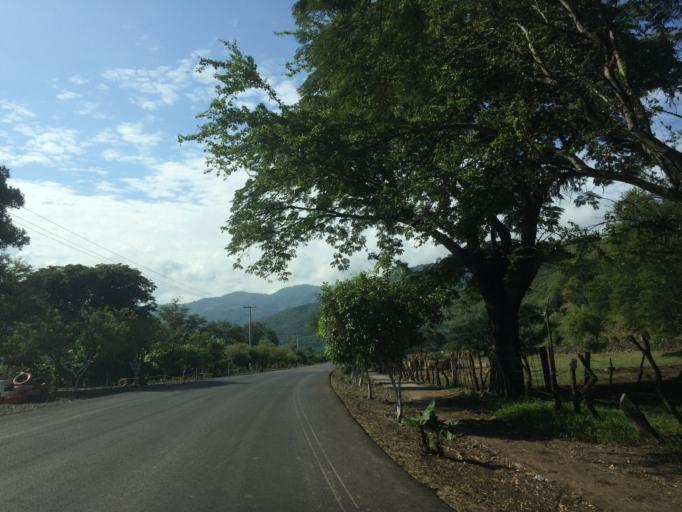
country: MX
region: Nayarit
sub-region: Ahuacatlan
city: Ahuacatlan
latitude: 21.0456
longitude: -104.4725
